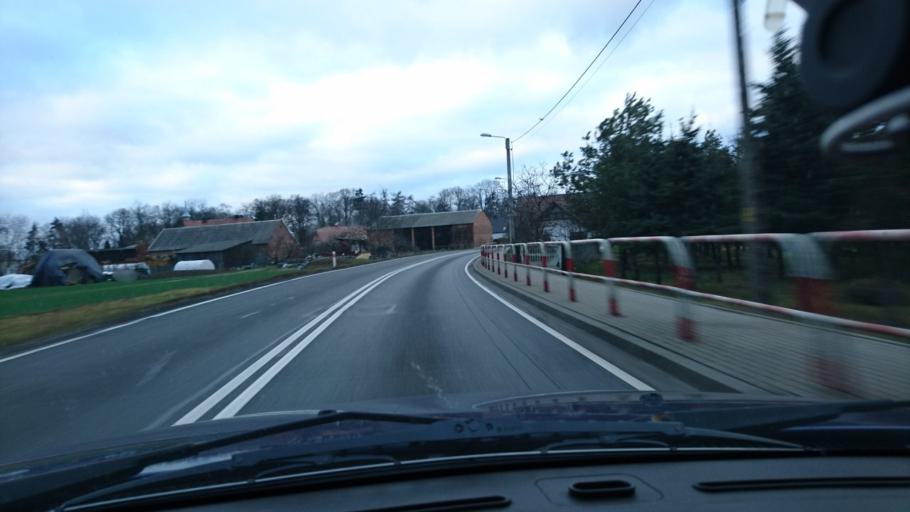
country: PL
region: Greater Poland Voivodeship
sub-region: Powiat kepinski
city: Opatow
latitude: 51.1778
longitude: 18.1433
